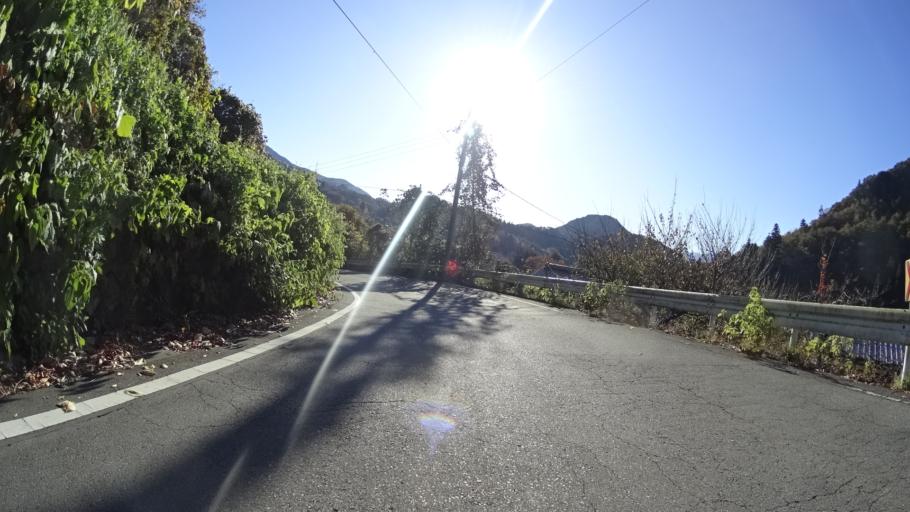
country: JP
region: Yamanashi
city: Uenohara
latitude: 35.6755
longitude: 139.0874
